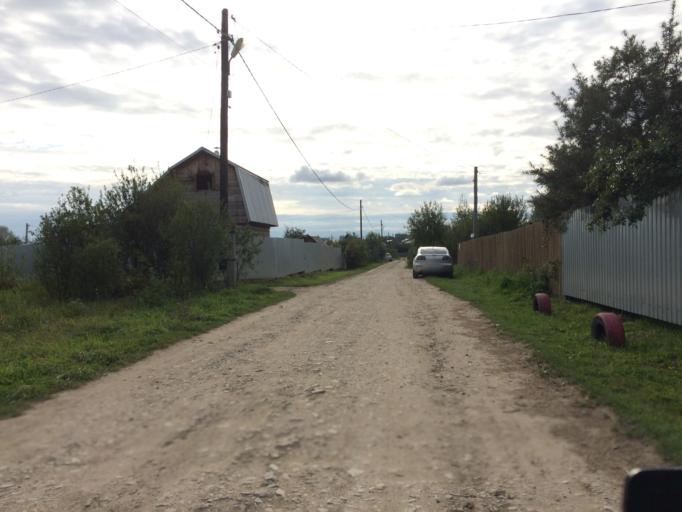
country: RU
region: Mariy-El
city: Yoshkar-Ola
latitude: 56.6550
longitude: 48.0006
